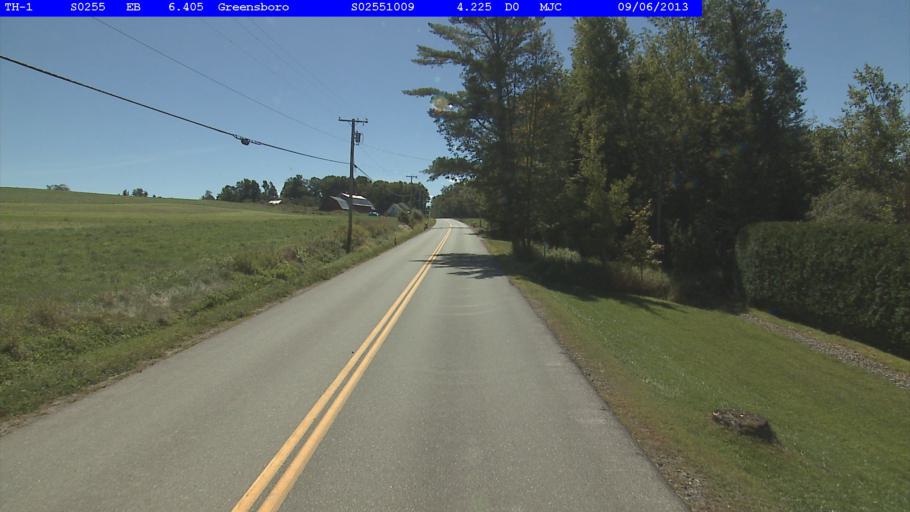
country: US
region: Vermont
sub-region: Caledonia County
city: Hardwick
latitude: 44.5878
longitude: -72.2985
